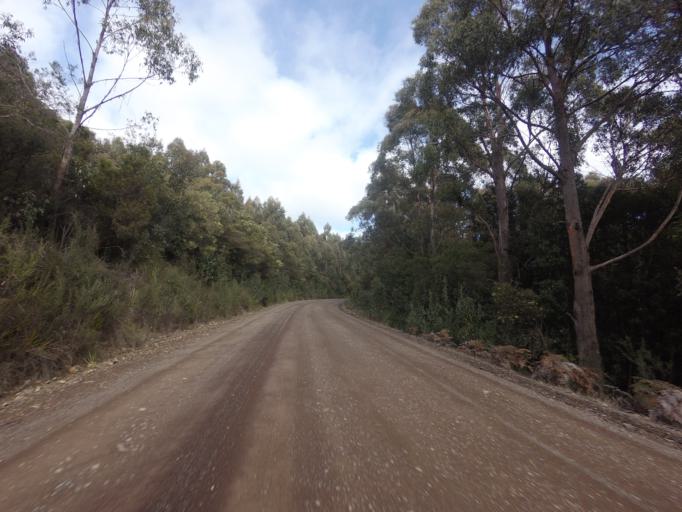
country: AU
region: Tasmania
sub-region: Huon Valley
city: Geeveston
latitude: -43.4680
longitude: 146.8974
